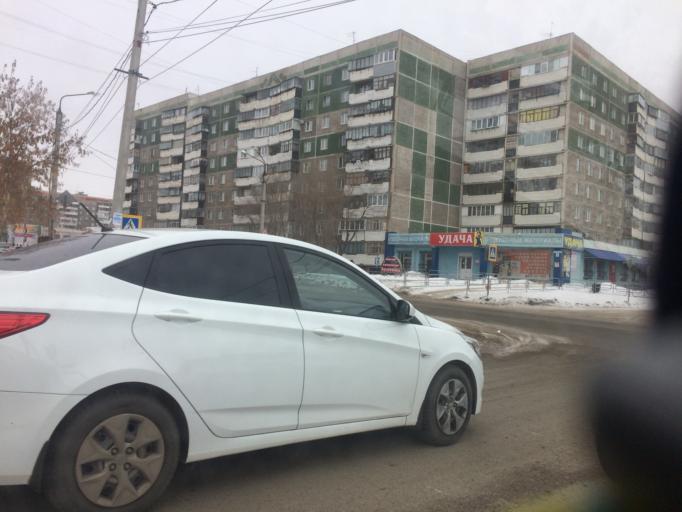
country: RU
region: Chelyabinsk
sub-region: Gorod Magnitogorsk
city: Magnitogorsk
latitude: 53.3600
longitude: 58.9995
